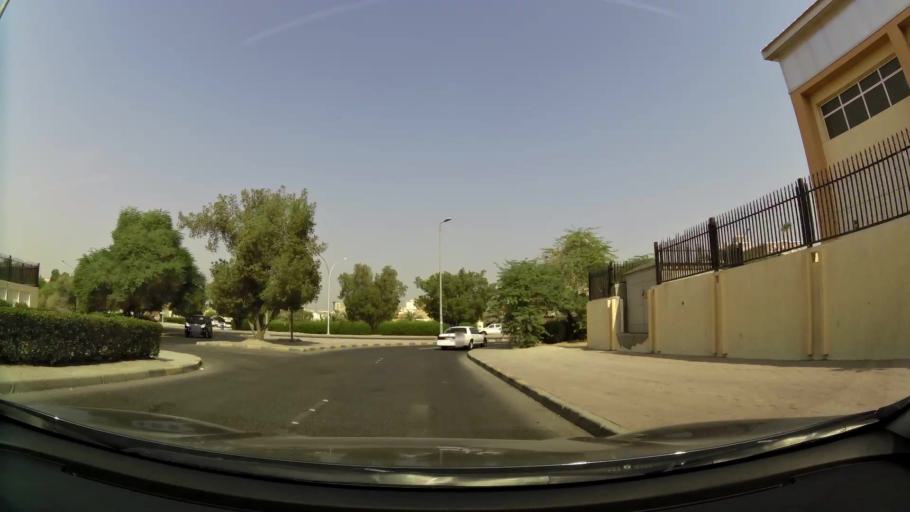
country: KW
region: Al Asimah
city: Ar Rabiyah
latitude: 29.2890
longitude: 47.8903
